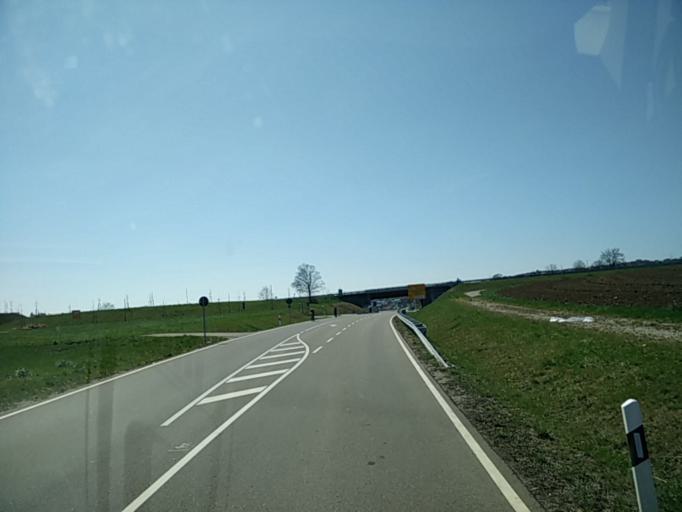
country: DE
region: Baden-Wuerttemberg
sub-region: Tuebingen Region
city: Dusslingen
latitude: 48.4577
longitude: 9.0650
